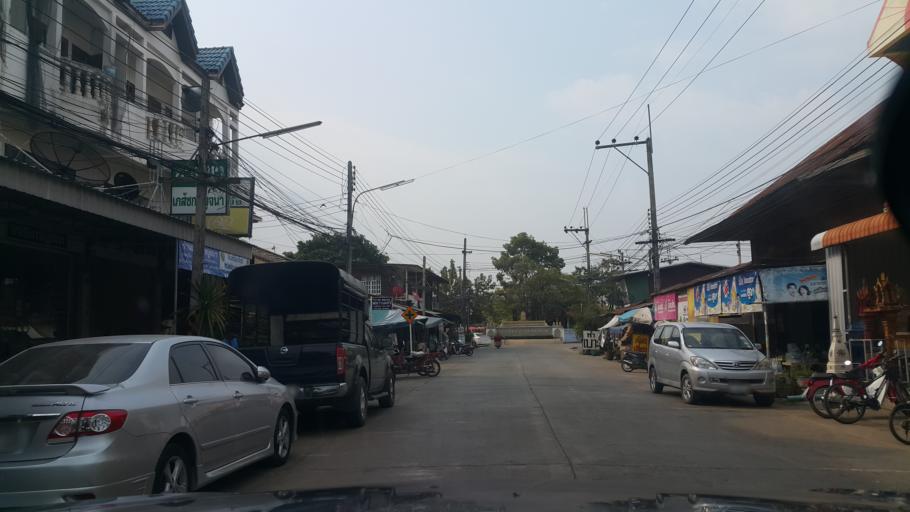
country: TH
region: Sukhothai
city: Si Samrong
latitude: 17.1662
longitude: 99.8610
